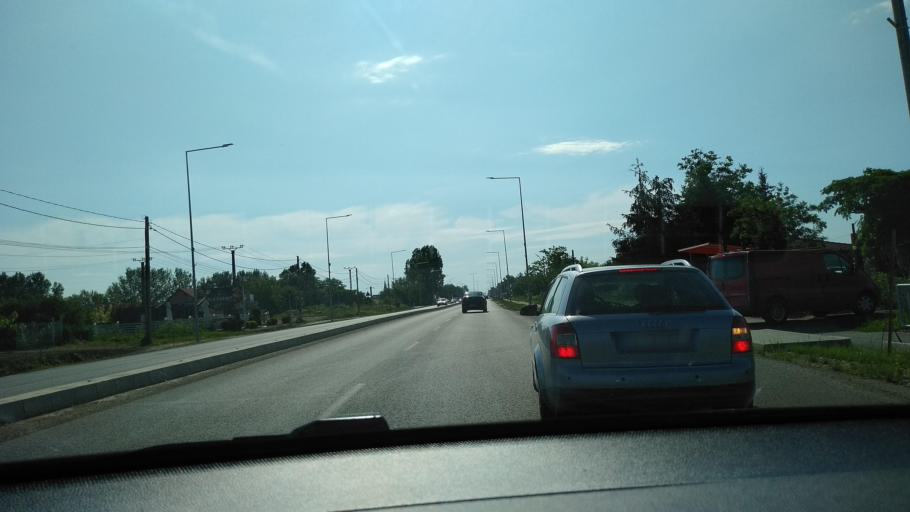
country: RO
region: Timis
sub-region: Comuna Mosnita Noua
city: Mosnita Noua
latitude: 45.7209
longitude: 21.3107
